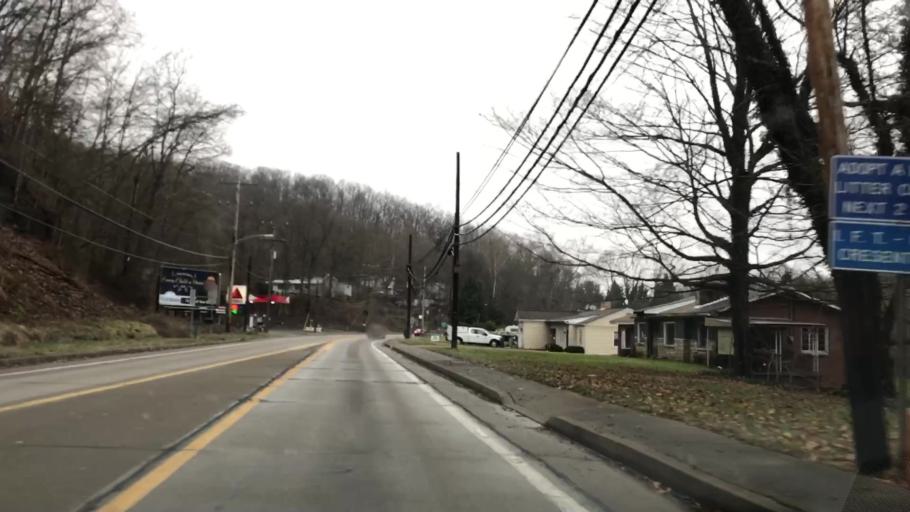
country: US
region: Pennsylvania
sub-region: Allegheny County
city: Leetsdale
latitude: 40.5443
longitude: -80.2182
